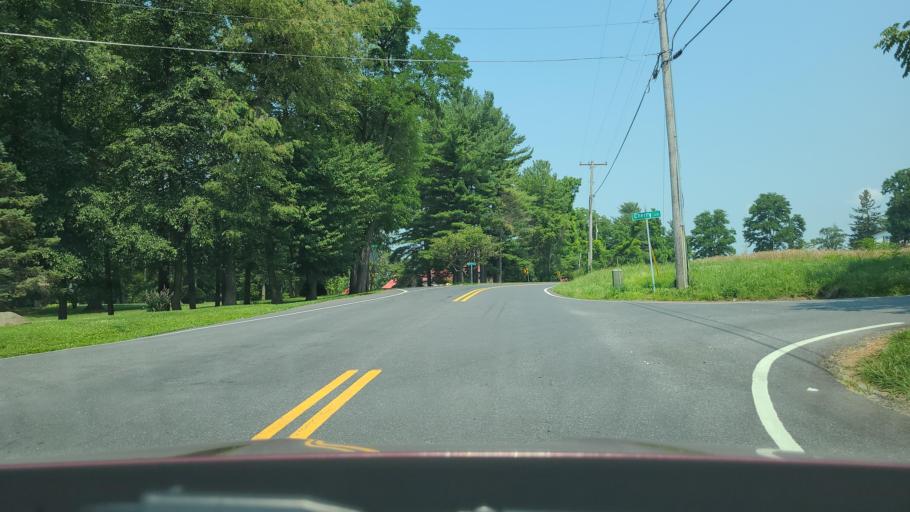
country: US
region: Maryland
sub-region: Frederick County
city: Braddock Heights
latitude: 39.3965
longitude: -77.5232
